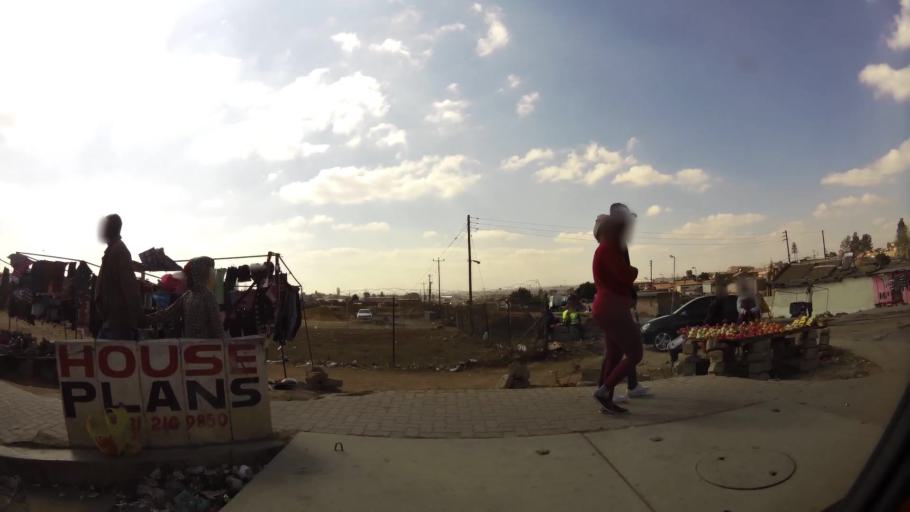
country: ZA
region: Gauteng
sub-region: Ekurhuleni Metropolitan Municipality
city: Tembisa
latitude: -26.0049
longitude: 28.1797
